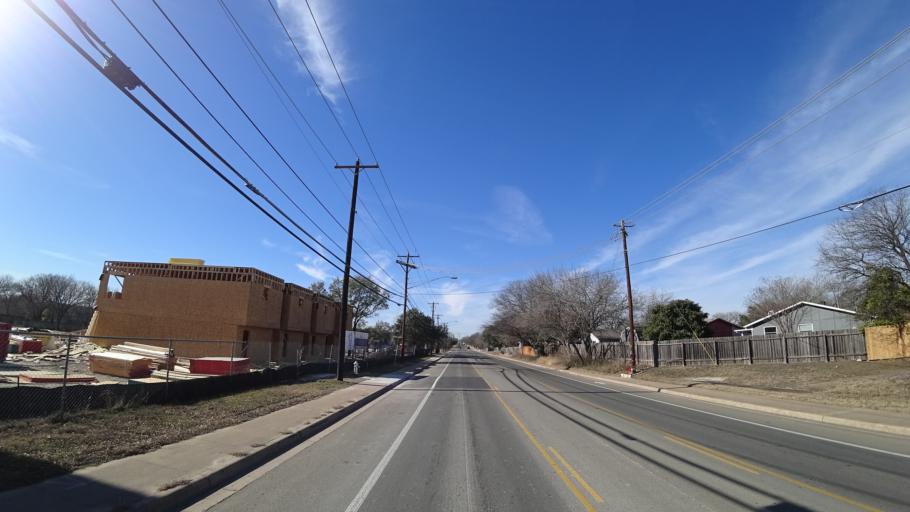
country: US
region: Texas
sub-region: Travis County
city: Wells Branch
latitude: 30.3833
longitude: -97.6993
